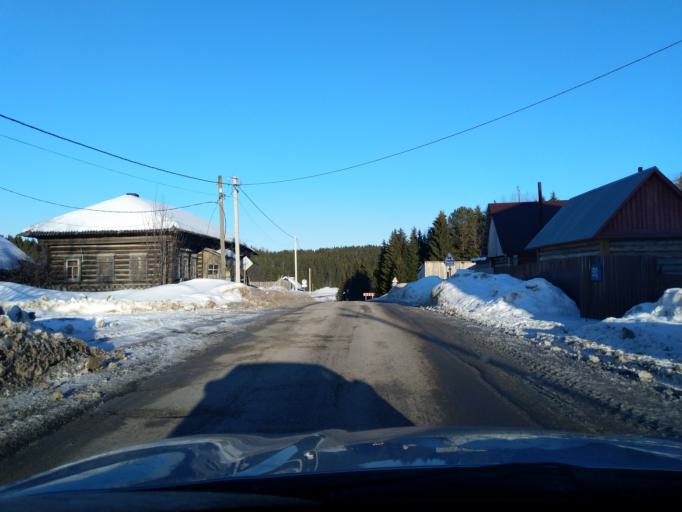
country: RU
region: Perm
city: Polazna
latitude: 58.3084
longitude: 56.4583
